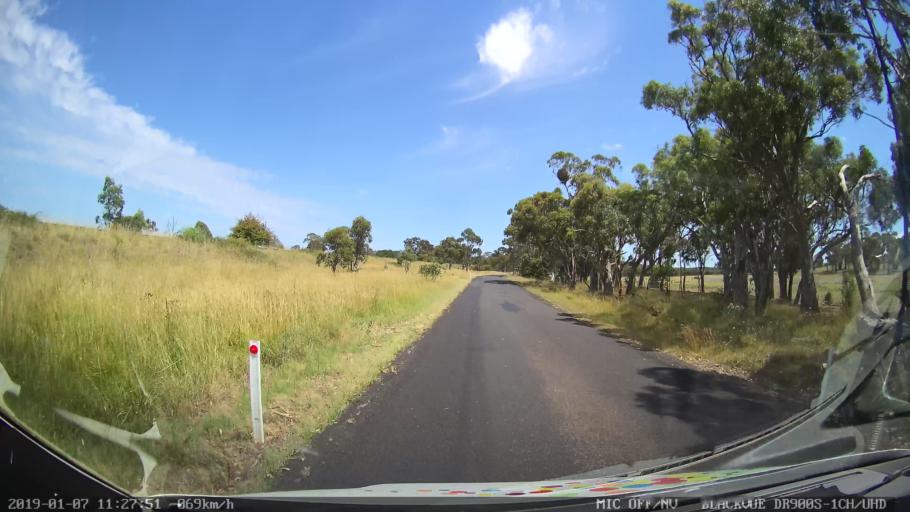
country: AU
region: New South Wales
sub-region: Armidale Dumaresq
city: Armidale
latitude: -30.4540
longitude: 151.5702
